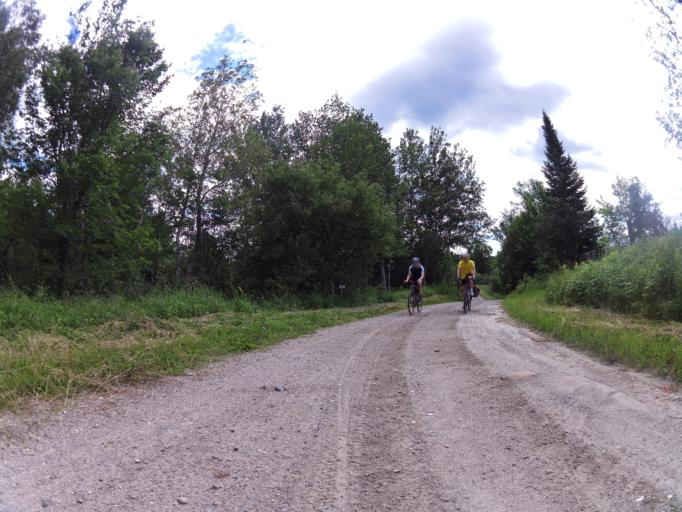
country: CA
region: Ontario
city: Perth
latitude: 45.0270
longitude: -76.5464
